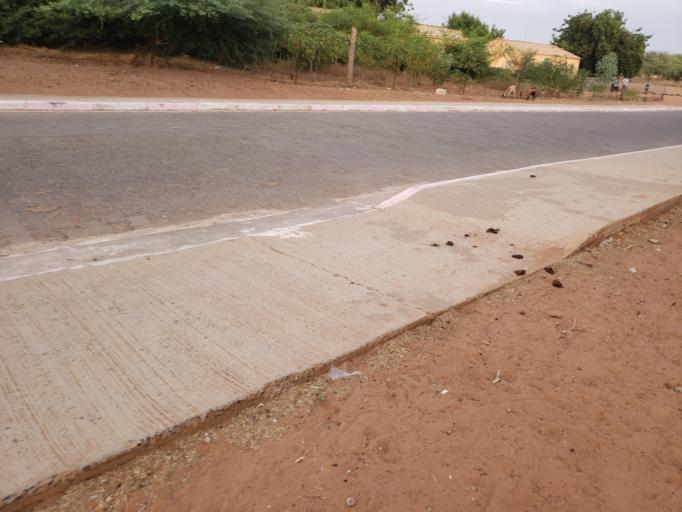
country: SN
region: Louga
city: Ndibene Dahra
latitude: 15.3990
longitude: -15.1117
